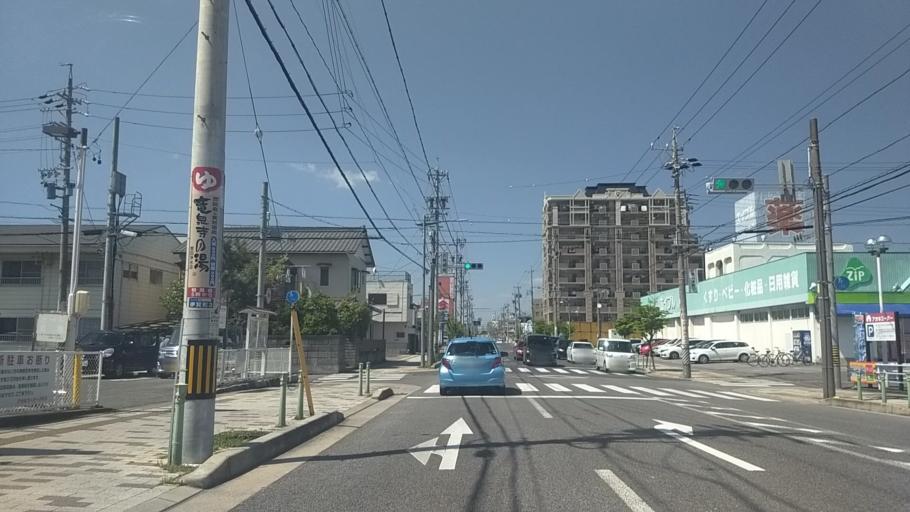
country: JP
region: Aichi
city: Okazaki
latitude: 34.9690
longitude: 137.1713
